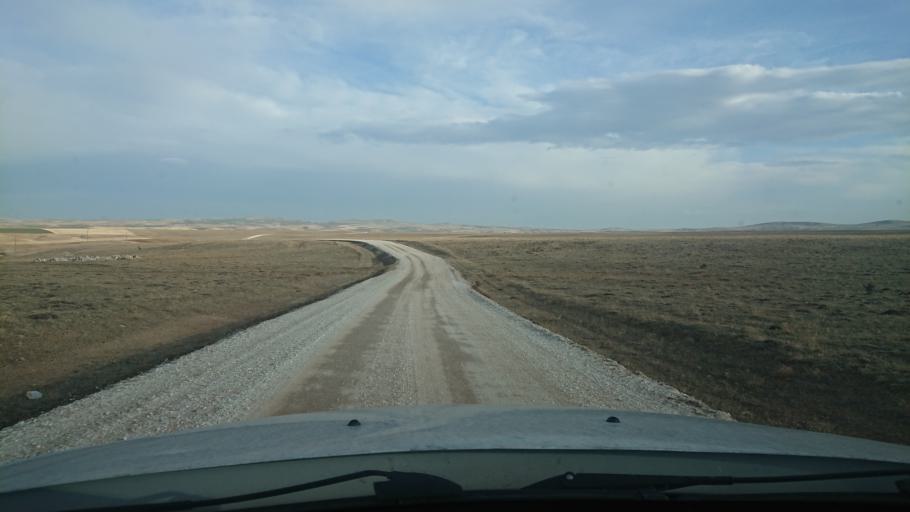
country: TR
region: Aksaray
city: Agacoren
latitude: 38.7291
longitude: 33.8692
